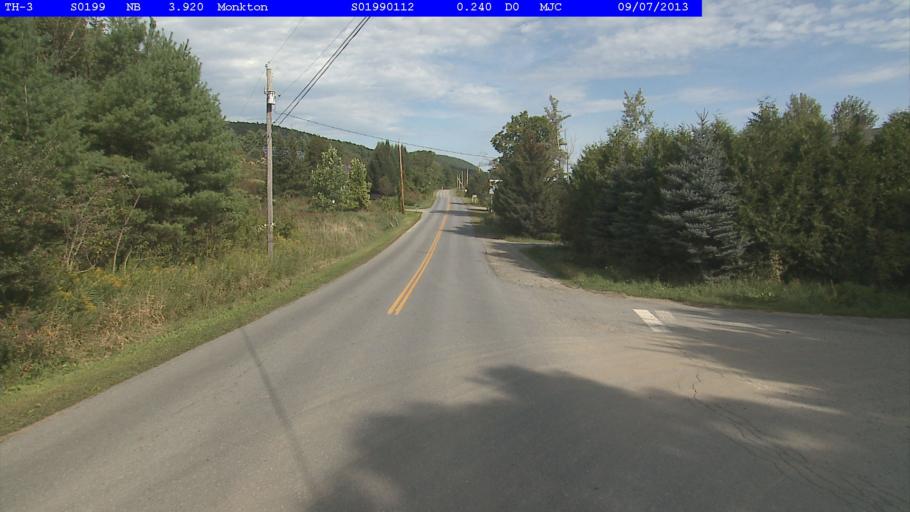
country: US
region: Vermont
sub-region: Addison County
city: Bristol
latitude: 44.1842
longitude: -73.1060
